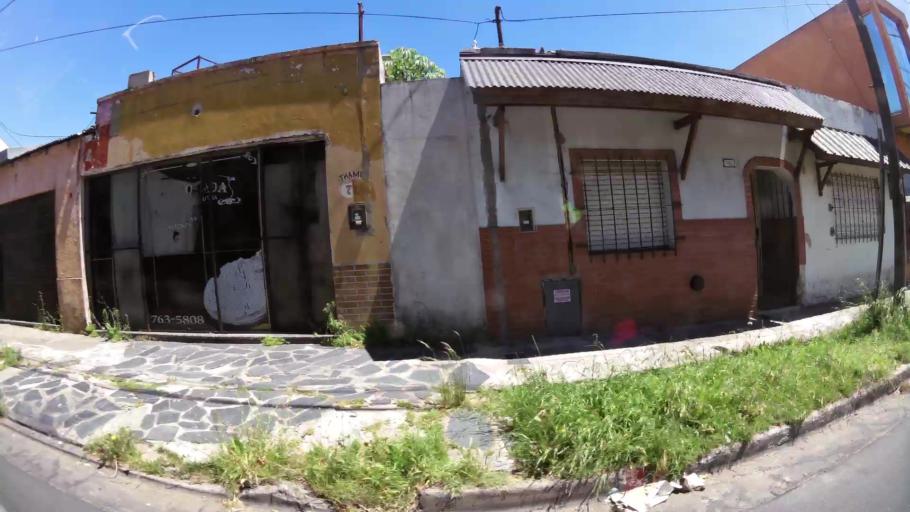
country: AR
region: Buenos Aires
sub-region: Partido de San Isidro
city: San Isidro
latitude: -34.5033
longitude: -58.5485
